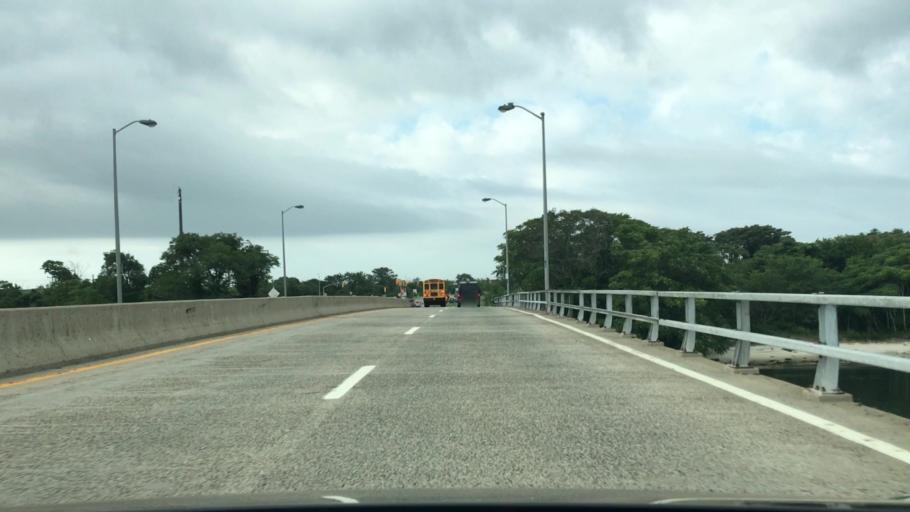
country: US
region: New York
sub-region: Nassau County
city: Point Lookout
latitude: 40.5941
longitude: -73.5873
